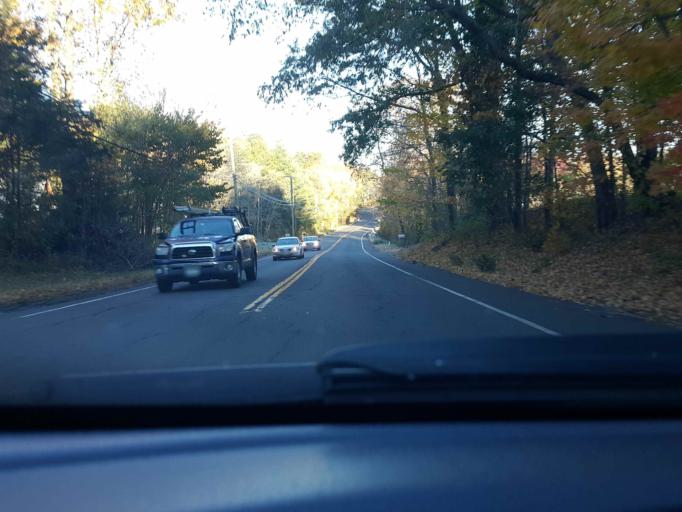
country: US
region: Connecticut
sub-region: New Haven County
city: Seymour
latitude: 41.3899
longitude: -73.0351
